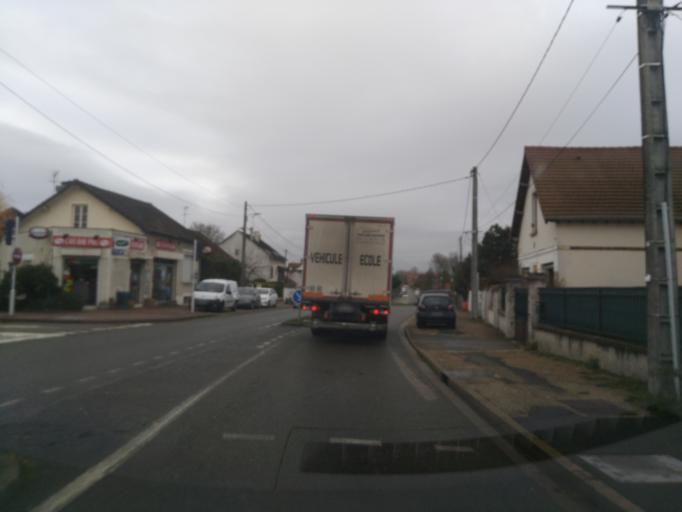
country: FR
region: Ile-de-France
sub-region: Departement des Yvelines
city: Villepreux
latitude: 48.8195
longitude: 2.0013
